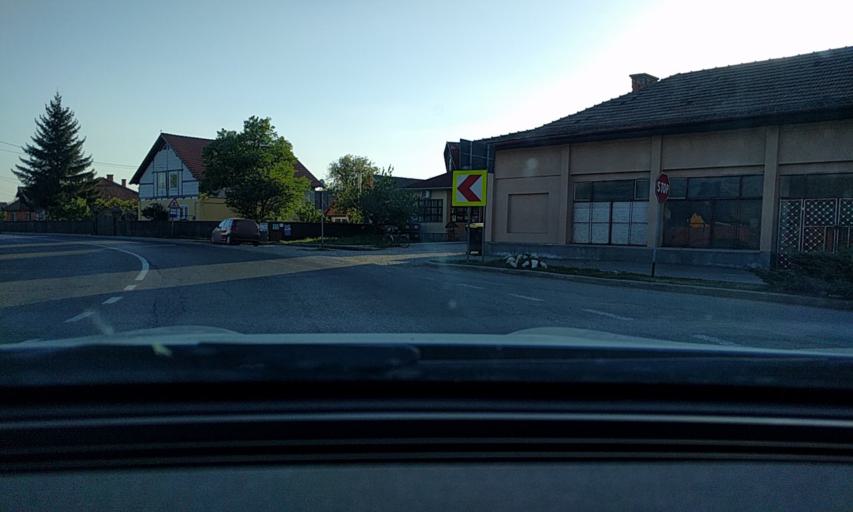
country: RO
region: Covasna
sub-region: Comuna Lemnia
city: Lemnia
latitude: 46.0467
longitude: 26.2657
